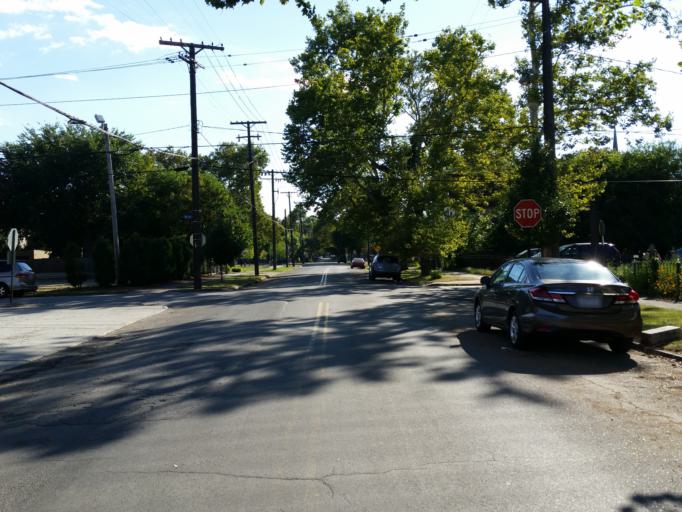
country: US
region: Ohio
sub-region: Cuyahoga County
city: Cleveland
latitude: 41.4824
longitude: -81.7029
